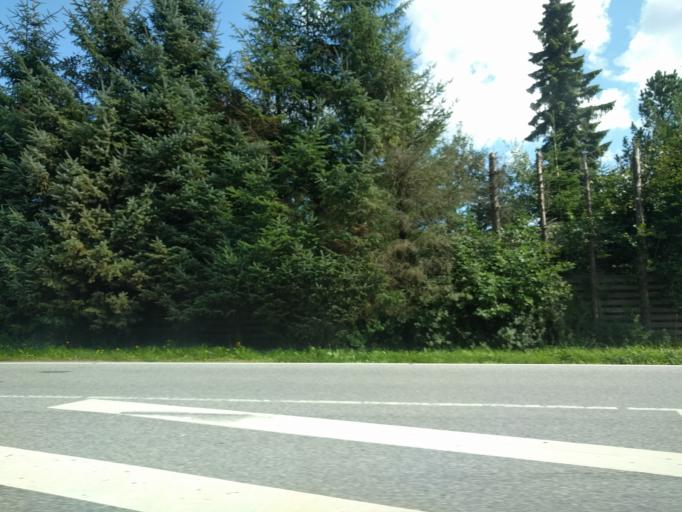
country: DK
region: Central Jutland
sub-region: Skive Kommune
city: Skive
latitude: 56.5893
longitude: 9.0294
